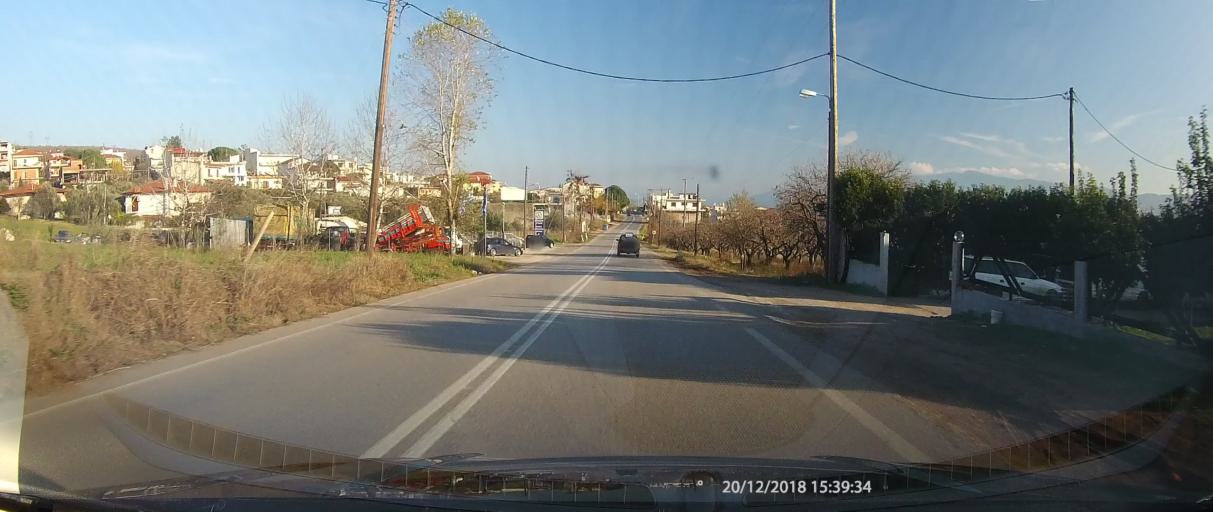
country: GR
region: Central Greece
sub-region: Nomos Fthiotidos
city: Stavros
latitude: 38.8955
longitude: 22.3667
